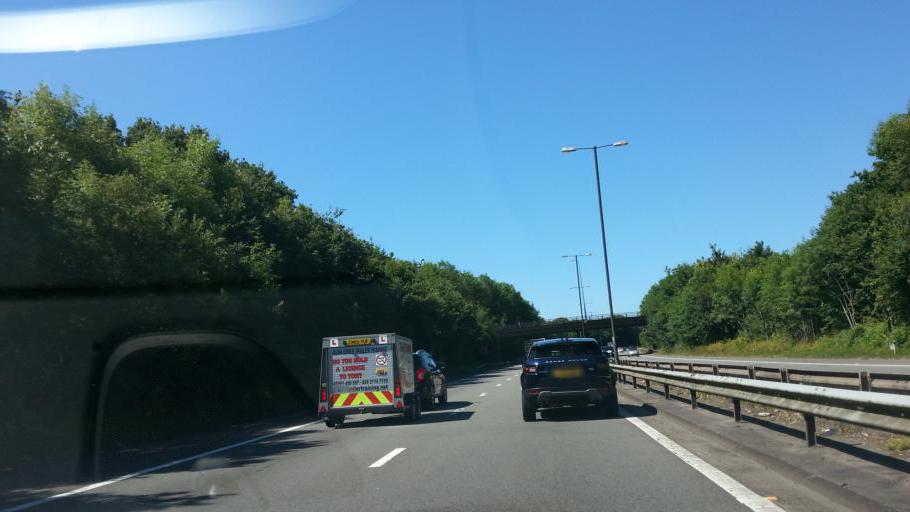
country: GB
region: Wales
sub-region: Newport
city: Marshfield
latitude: 51.5332
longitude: -3.1022
